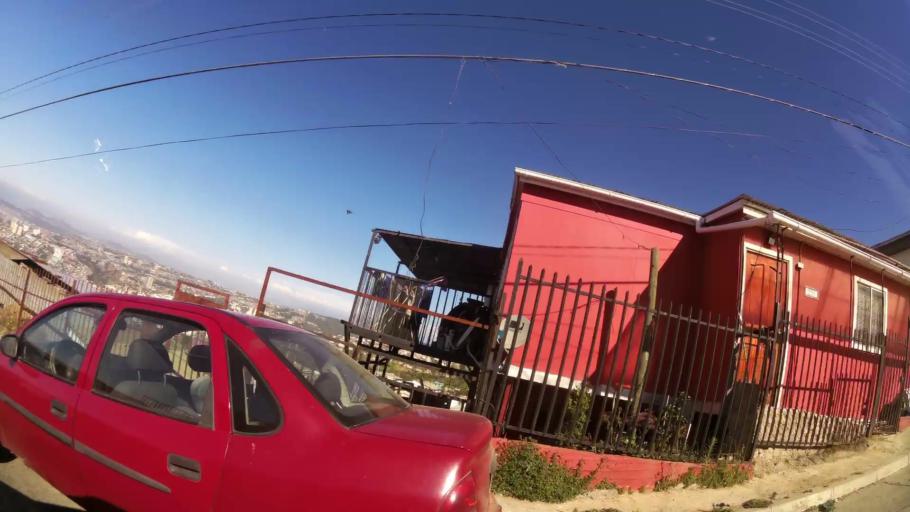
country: CL
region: Valparaiso
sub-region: Provincia de Valparaiso
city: Valparaiso
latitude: -33.0614
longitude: -71.6222
